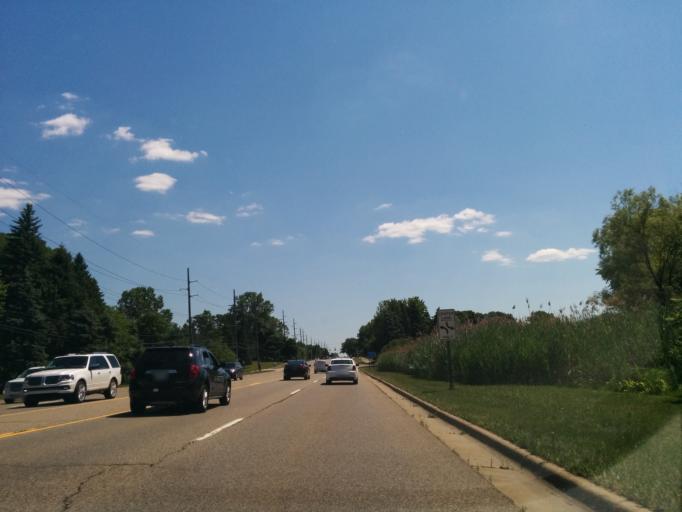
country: US
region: Michigan
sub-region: Oakland County
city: Orchard Lake
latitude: 42.5613
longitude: -83.3617
